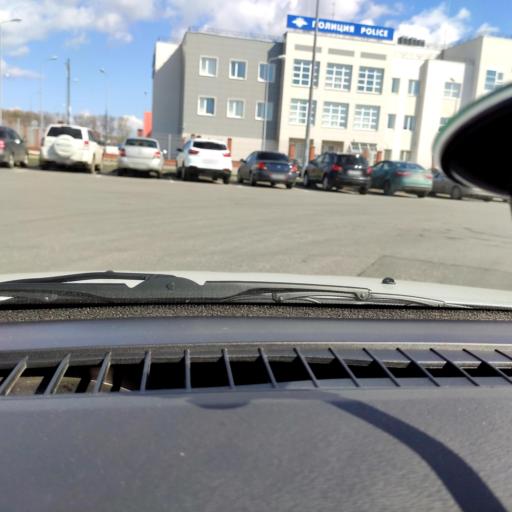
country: RU
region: Samara
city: Petra-Dubrava
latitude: 53.2761
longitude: 50.2533
